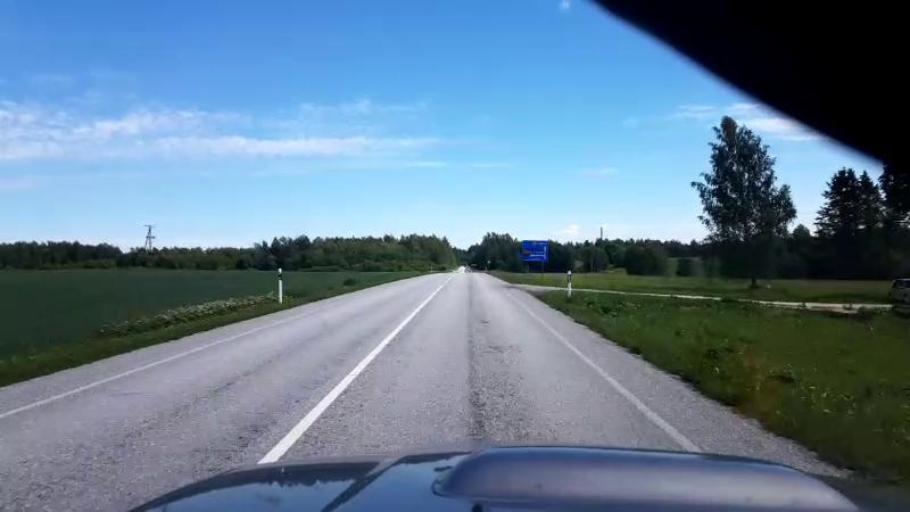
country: EE
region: Laeaene-Virumaa
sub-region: Rakke vald
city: Rakke
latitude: 58.9175
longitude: 26.2553
